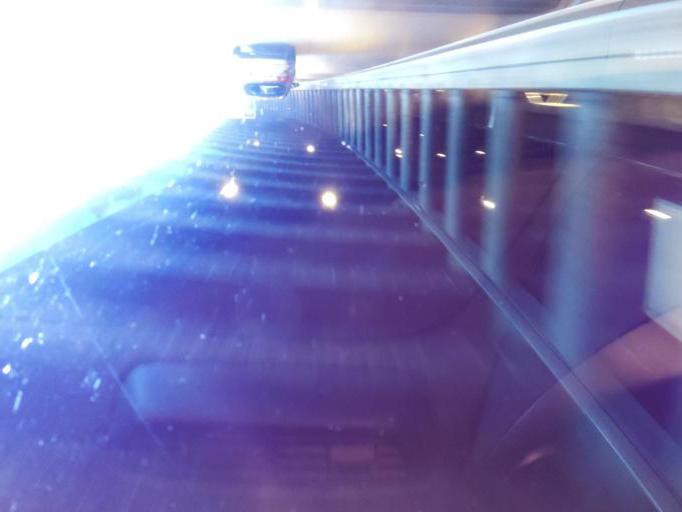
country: AT
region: Tyrol
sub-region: Politischer Bezirk Innsbruck Land
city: Schoenberg im Stubaital
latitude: 47.1872
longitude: 11.4017
